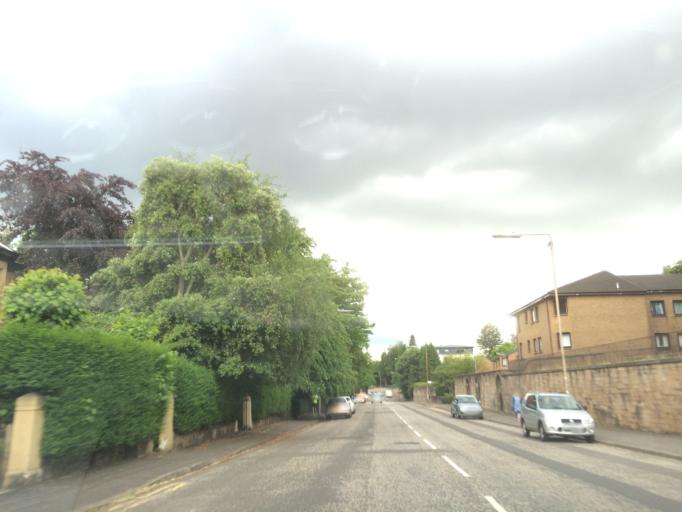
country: GB
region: Scotland
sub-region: East Renfrewshire
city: Giffnock
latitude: 55.8261
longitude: -4.2727
